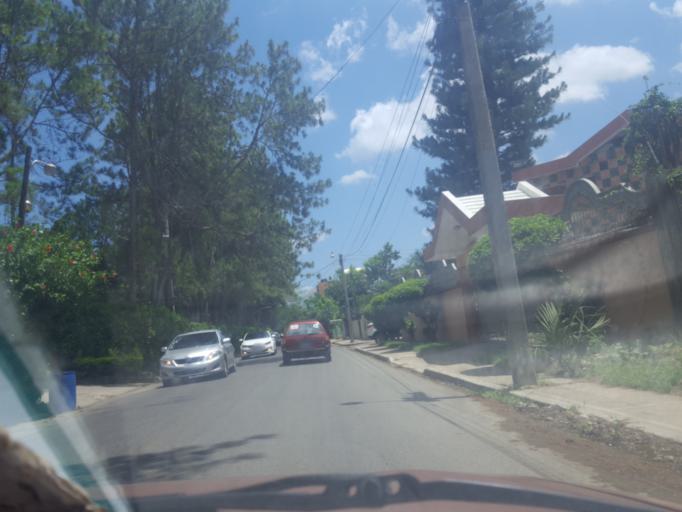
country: DO
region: Santiago
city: Santiago de los Caballeros
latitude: 19.4784
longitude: -70.6596
